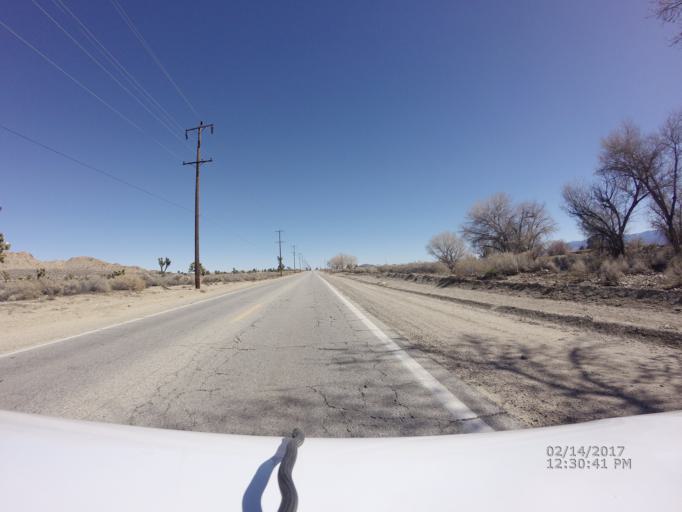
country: US
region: California
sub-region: Los Angeles County
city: Lake Los Angeles
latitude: 34.5800
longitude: -117.8691
